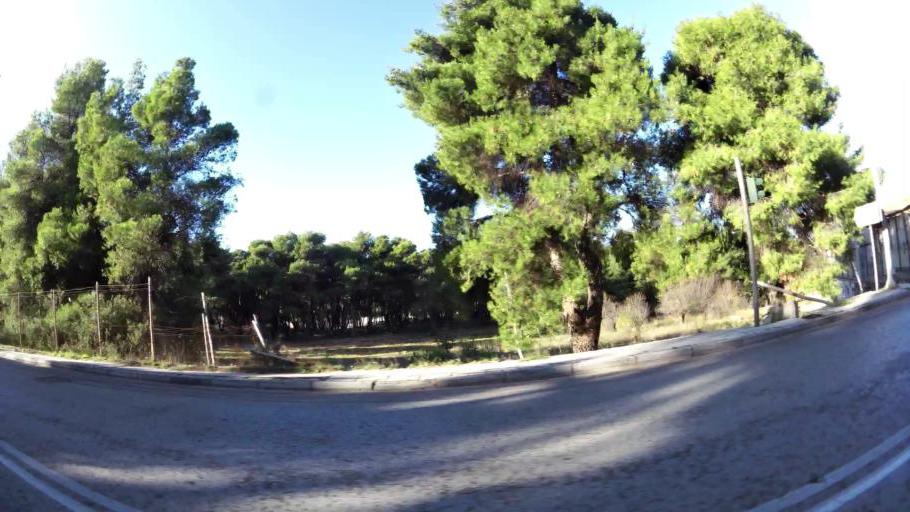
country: GR
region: Attica
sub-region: Nomarchia Anatolikis Attikis
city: Drosia
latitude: 38.1237
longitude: 23.8565
